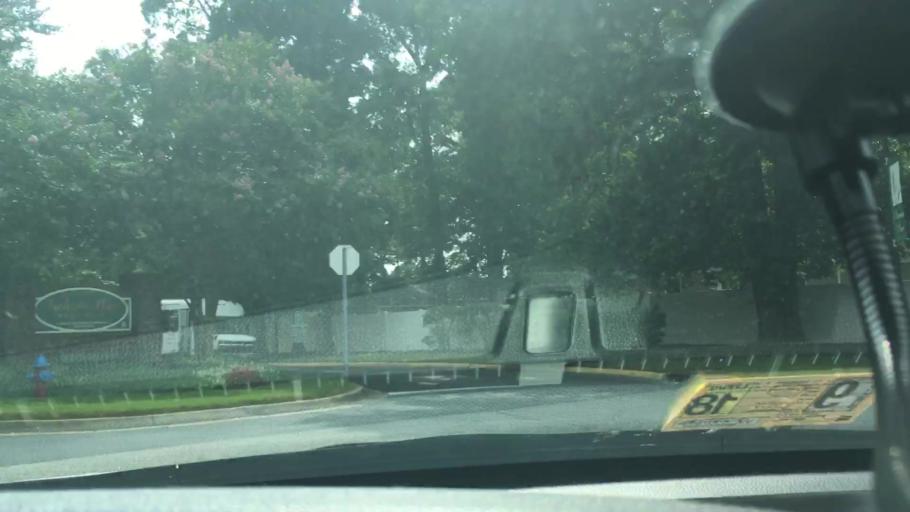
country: US
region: Virginia
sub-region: City of Virginia Beach
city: Virginia Beach
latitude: 36.9026
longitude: -76.1312
